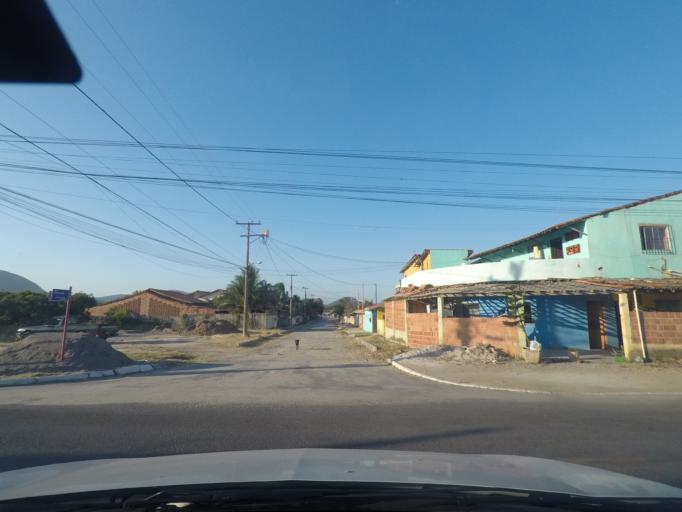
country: BR
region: Rio de Janeiro
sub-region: Marica
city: Marica
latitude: -22.9670
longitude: -42.9316
